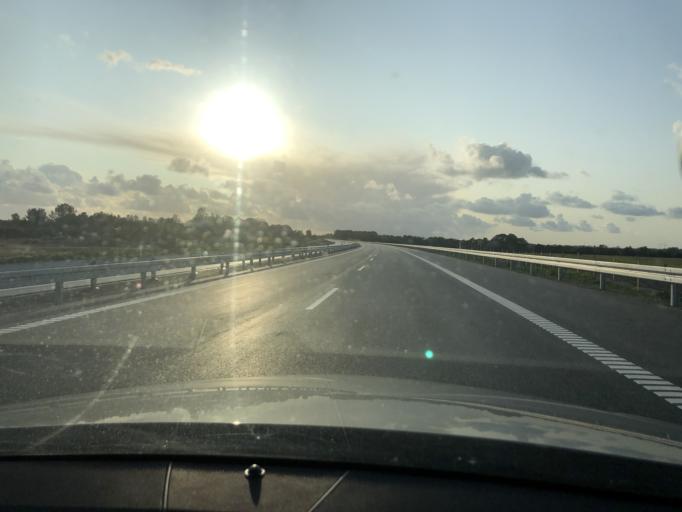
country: DK
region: Zealand
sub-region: Soro Kommune
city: Stenlille
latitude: 55.6614
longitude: 11.6042
